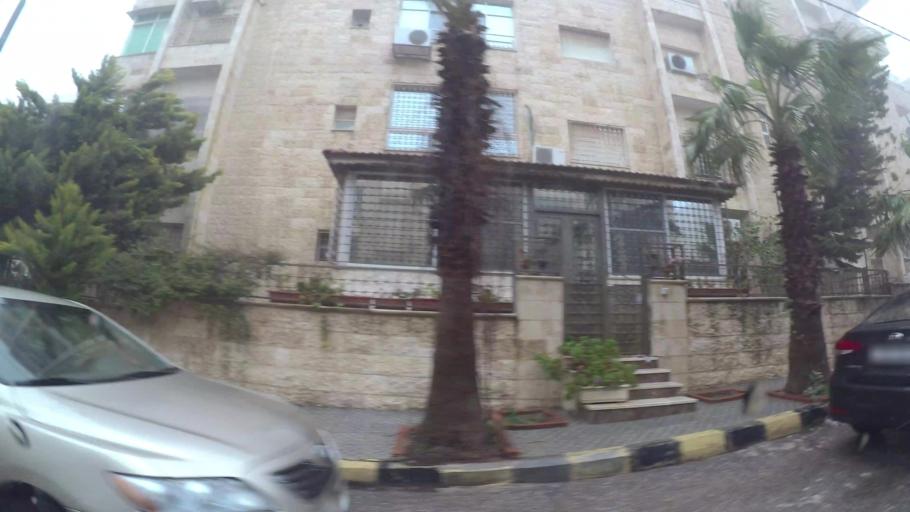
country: JO
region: Amman
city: Al Jubayhah
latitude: 32.0067
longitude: 35.8822
